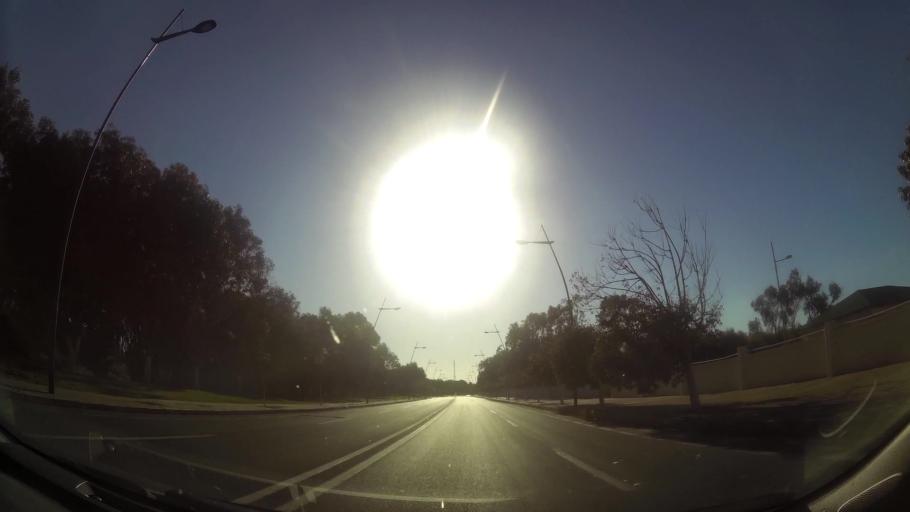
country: MA
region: Oriental
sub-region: Berkane-Taourirt
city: Madagh
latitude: 35.0900
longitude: -2.2469
